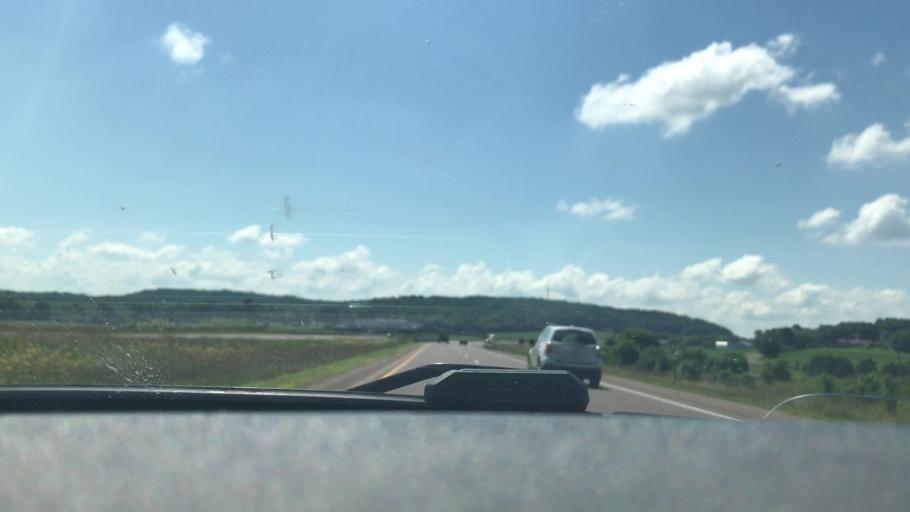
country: US
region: Wisconsin
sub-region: Chippewa County
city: Chippewa Falls
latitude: 44.9685
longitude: -91.4292
